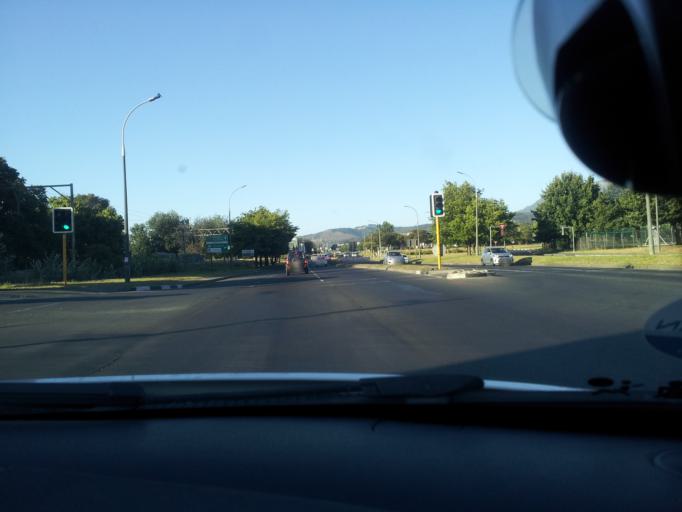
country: ZA
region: Western Cape
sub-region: Cape Winelands District Municipality
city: Stellenbosch
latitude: -33.9345
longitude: 18.8525
